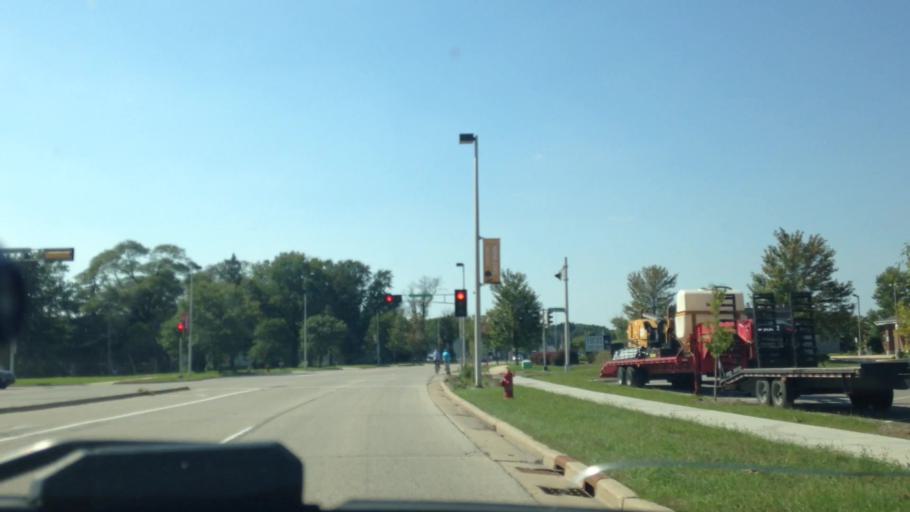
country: US
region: Wisconsin
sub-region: Waukesha County
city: Menomonee Falls
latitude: 43.1773
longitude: -88.0941
